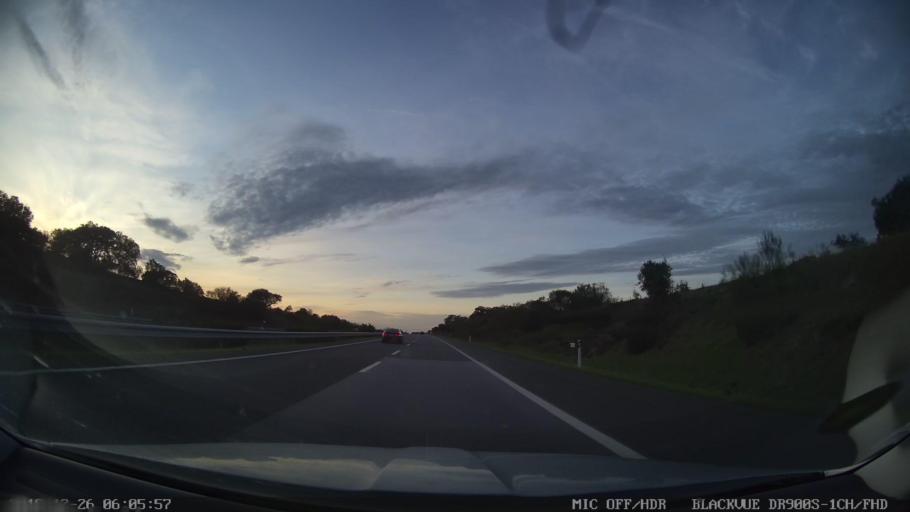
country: PT
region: Evora
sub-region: Montemor-O-Novo
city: Montemor-o-Novo
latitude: 38.6244
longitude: -8.0934
